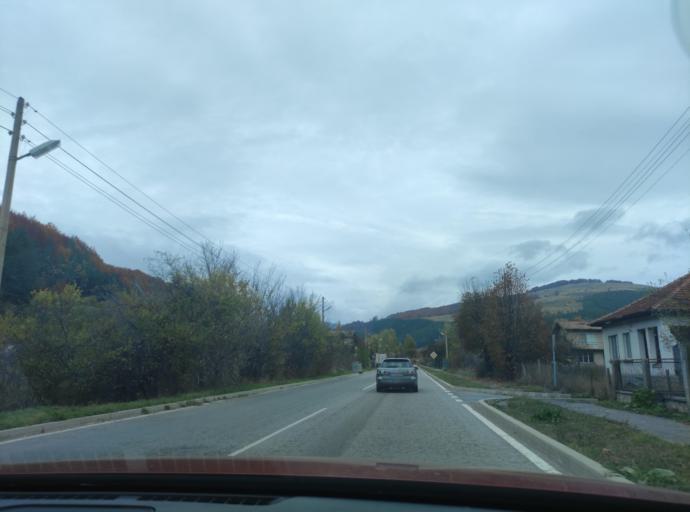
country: BG
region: Sofiya
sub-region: Obshtina Godech
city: Godech
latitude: 43.0755
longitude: 23.1079
